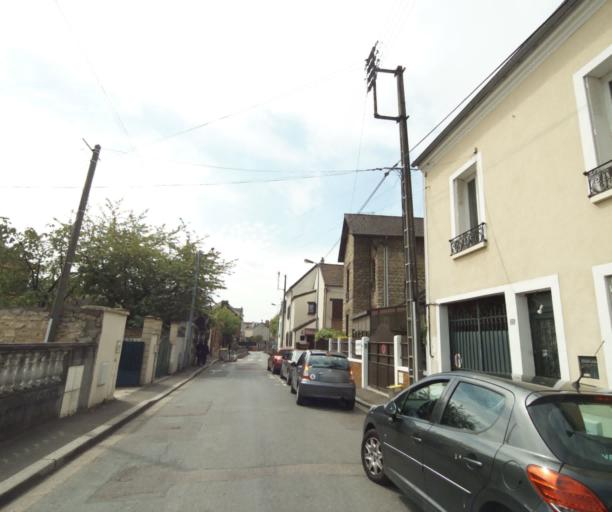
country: FR
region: Ile-de-France
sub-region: Departement des Yvelines
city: Les Mureaux
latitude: 48.9959
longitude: 1.9114
